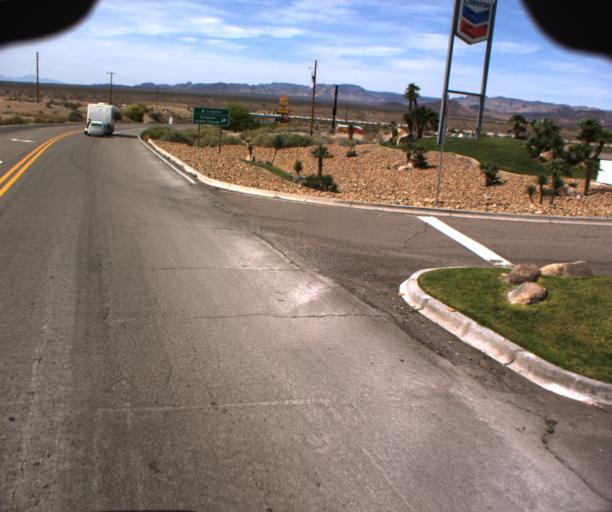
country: US
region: Arizona
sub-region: Mohave County
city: Desert Hills
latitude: 34.7265
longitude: -114.3159
